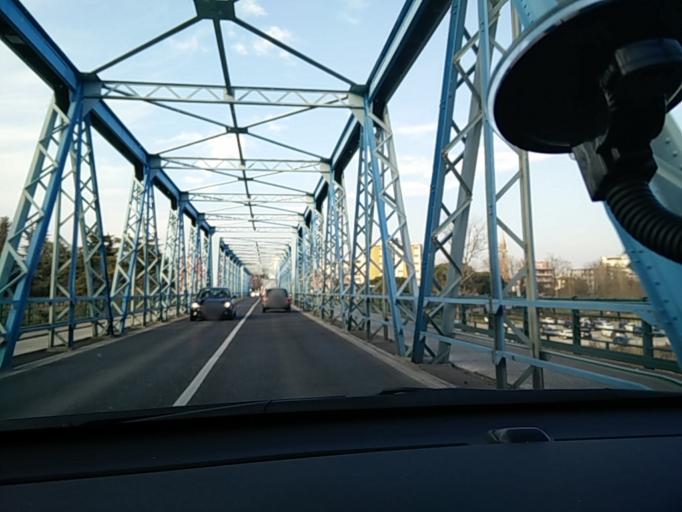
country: IT
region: Veneto
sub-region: Provincia di Venezia
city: San Dona di Piave
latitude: 45.6255
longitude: 12.5630
